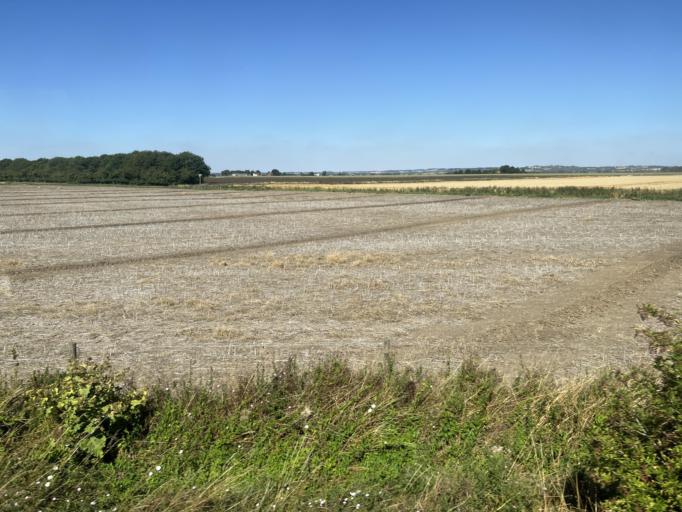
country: GB
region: England
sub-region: Lincolnshire
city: Spilsby
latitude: 53.0990
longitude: 0.1087
